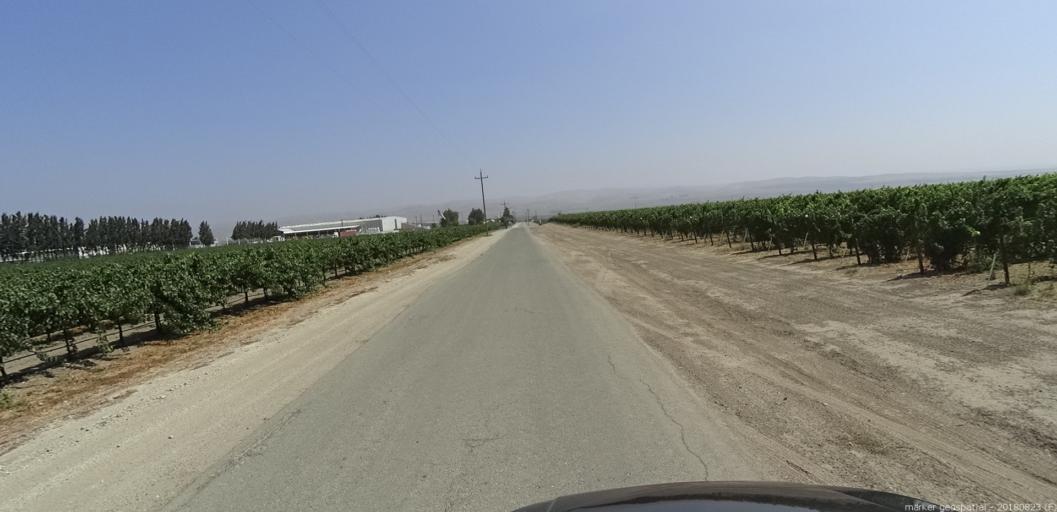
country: US
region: California
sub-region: Monterey County
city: Greenfield
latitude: 36.2728
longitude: -121.1912
